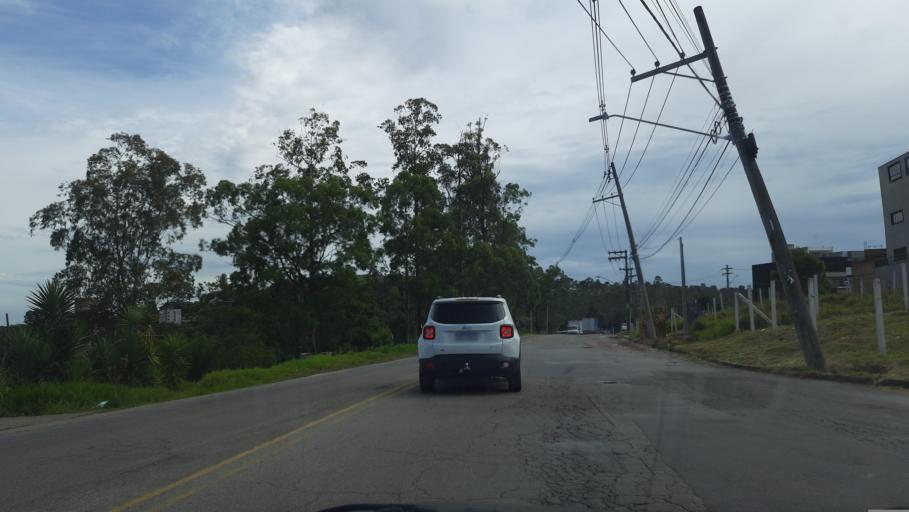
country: BR
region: Sao Paulo
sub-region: Caieiras
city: Caieiras
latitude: -23.3786
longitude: -46.7131
